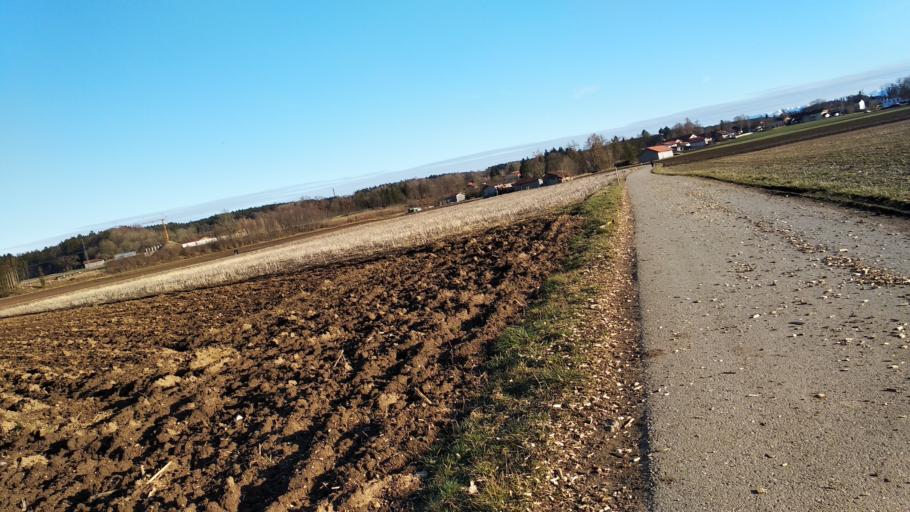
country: DE
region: Bavaria
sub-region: Upper Bavaria
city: Aying
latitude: 47.9792
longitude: 11.7731
